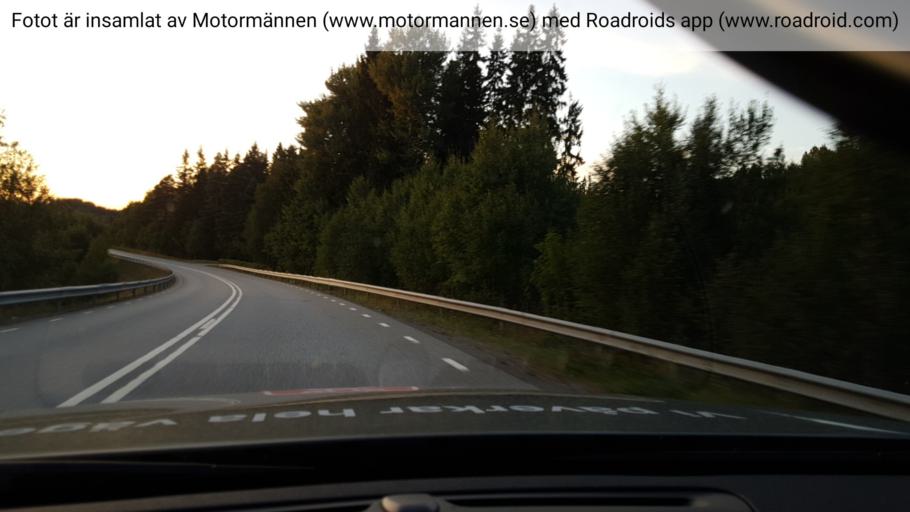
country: SE
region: OErebro
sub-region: Karlskoga Kommun
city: Karlskoga
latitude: 59.4518
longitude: 14.5084
